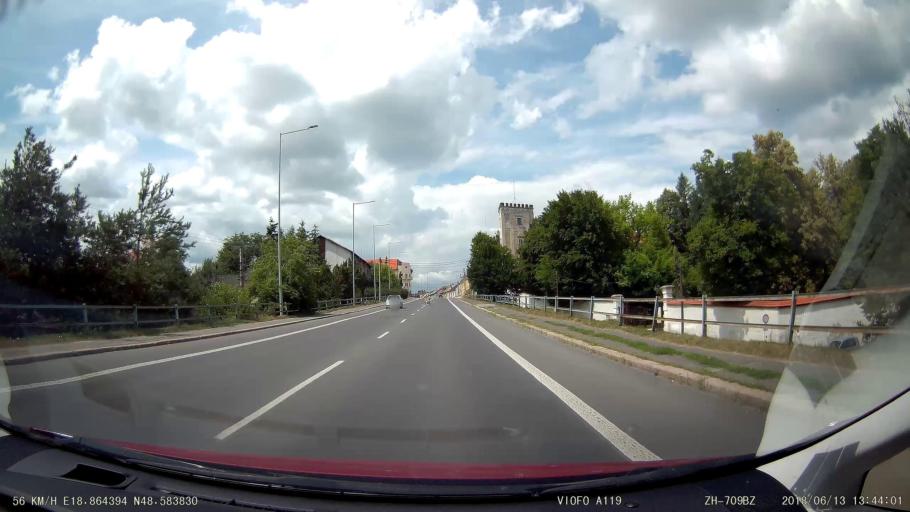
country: SK
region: Banskobystricky
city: Ziar nad Hronom
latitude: 48.5839
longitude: 18.8643
